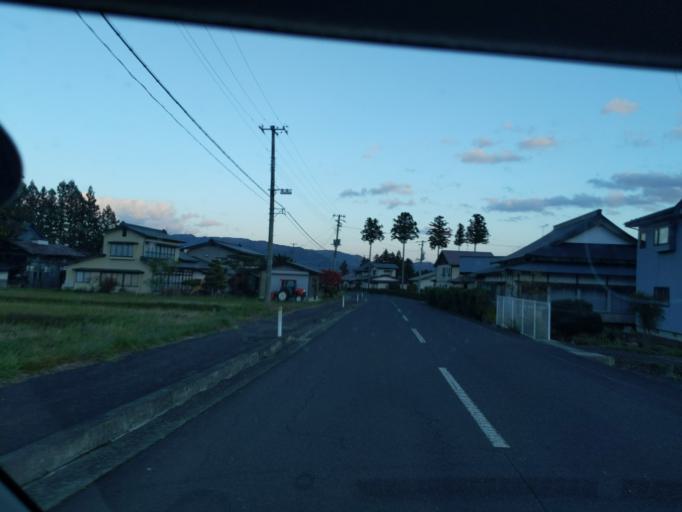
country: JP
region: Iwate
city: Ichinoseki
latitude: 39.0132
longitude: 141.0832
